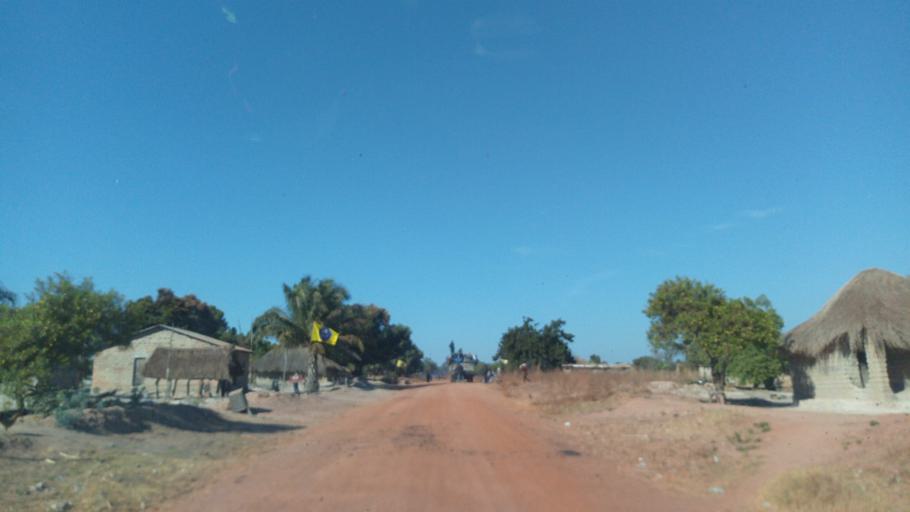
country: ZM
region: Luapula
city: Mwense
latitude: -10.6275
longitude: 28.4113
